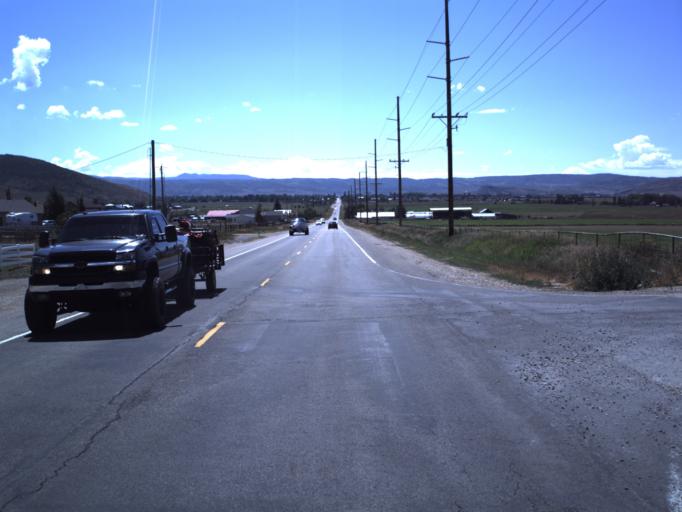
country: US
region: Utah
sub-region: Summit County
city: Kamas
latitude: 40.6751
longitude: -111.2809
